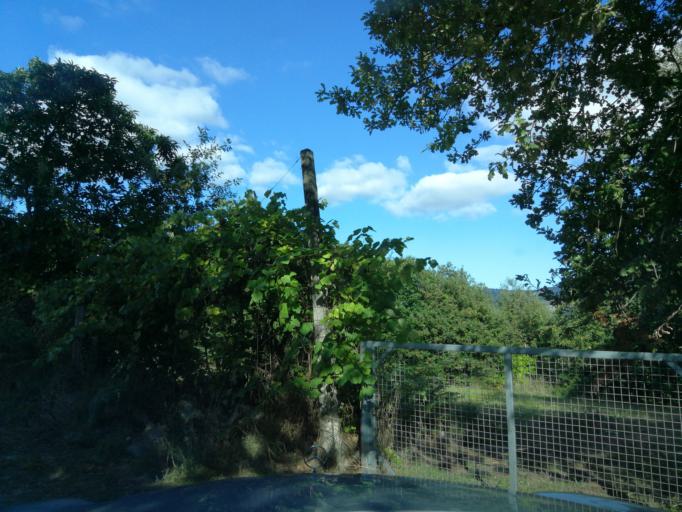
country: PT
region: Braga
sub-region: Braga
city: Adaufe
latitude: 41.5741
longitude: -8.3843
